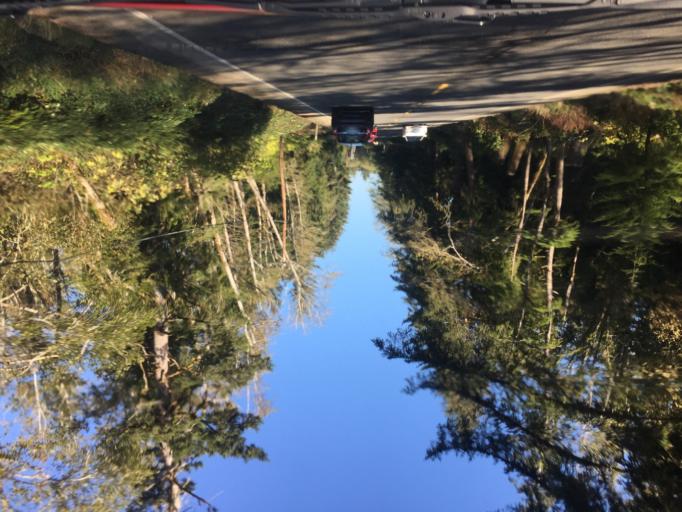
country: US
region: Oregon
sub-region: Clatsop County
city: Cannon Beach
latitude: 45.9042
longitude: -123.8751
